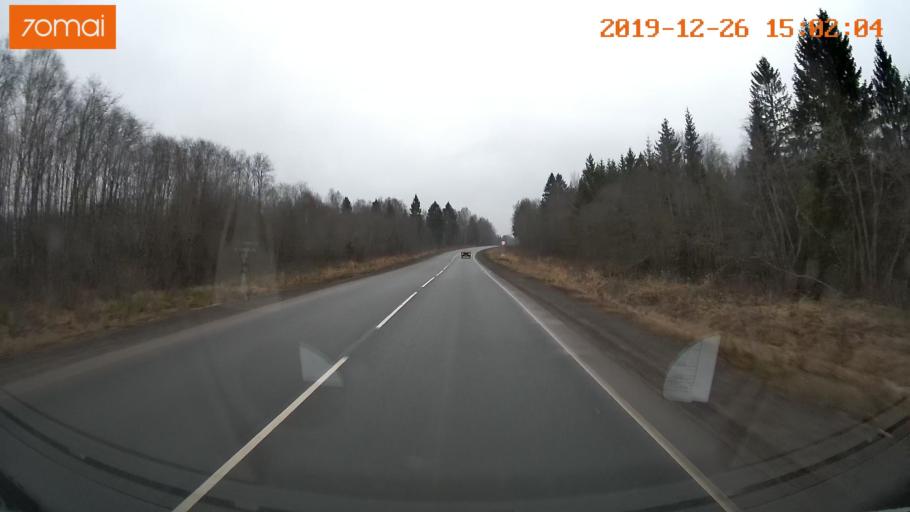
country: RU
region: Jaroslavl
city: Rybinsk
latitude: 58.2304
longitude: 38.8729
